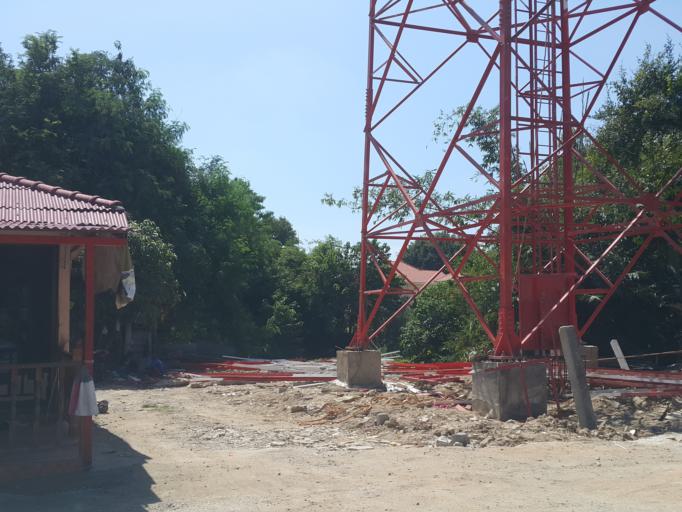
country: TH
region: Chiang Mai
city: Saraphi
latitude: 18.7597
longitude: 99.0508
